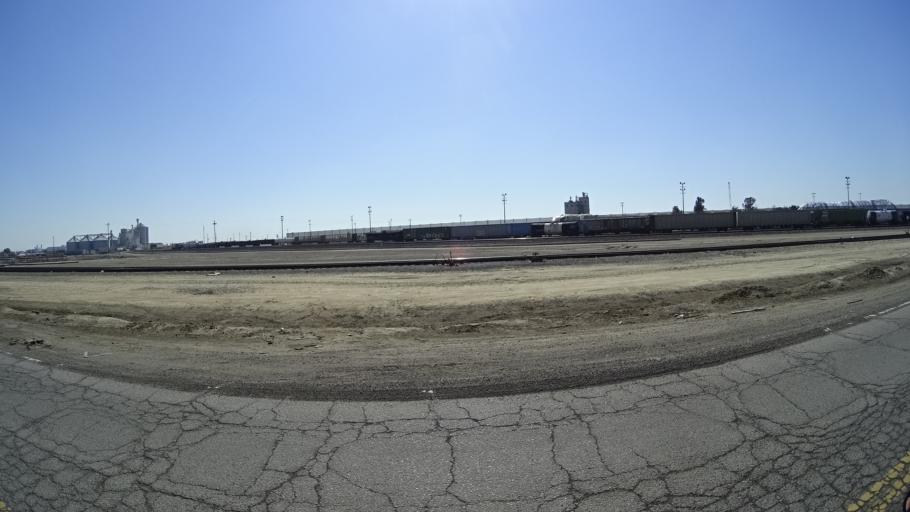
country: US
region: California
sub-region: Fresno County
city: Fresno
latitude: 36.7003
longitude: -119.7533
